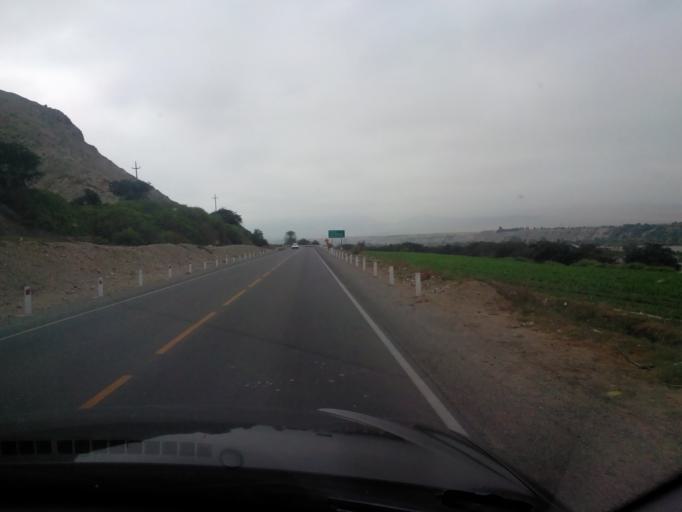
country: PE
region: Ica
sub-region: Provincia de Pisco
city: Humay
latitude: -13.7332
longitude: -75.9267
